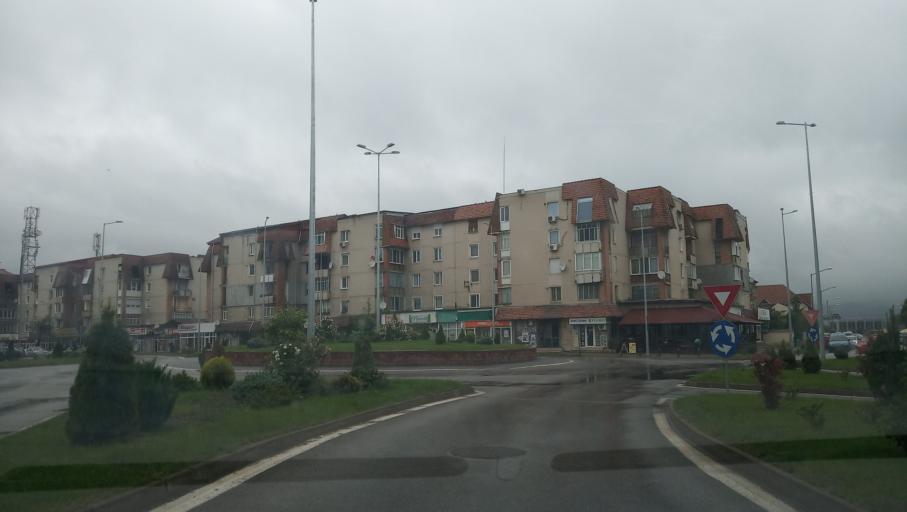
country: RO
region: Alba
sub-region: Municipiul Sebes
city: Sebes
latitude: 45.9551
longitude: 23.5783
